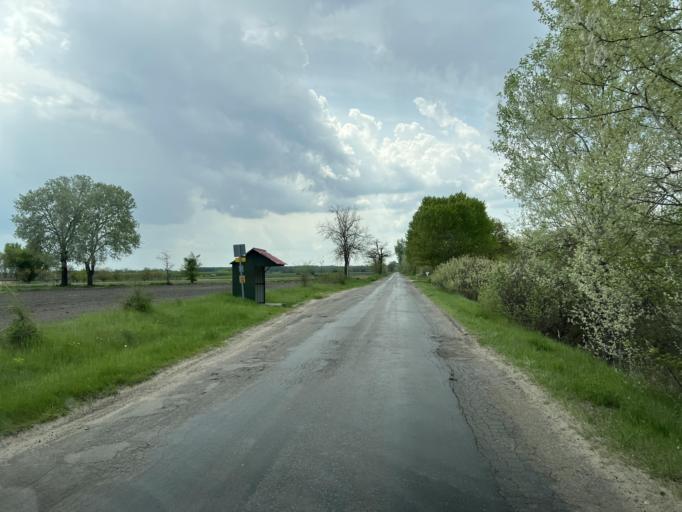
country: HU
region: Pest
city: Cegled
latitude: 47.1244
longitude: 19.7611
